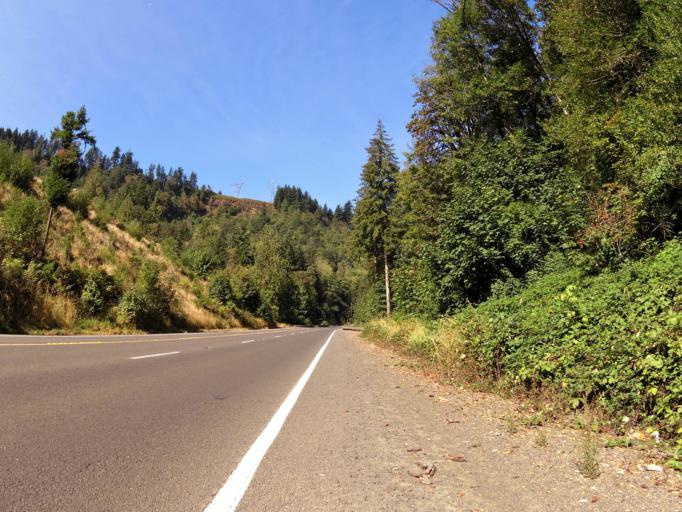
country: US
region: Washington
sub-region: Wahkiakum County
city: Cathlamet
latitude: 46.1574
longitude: -123.4254
